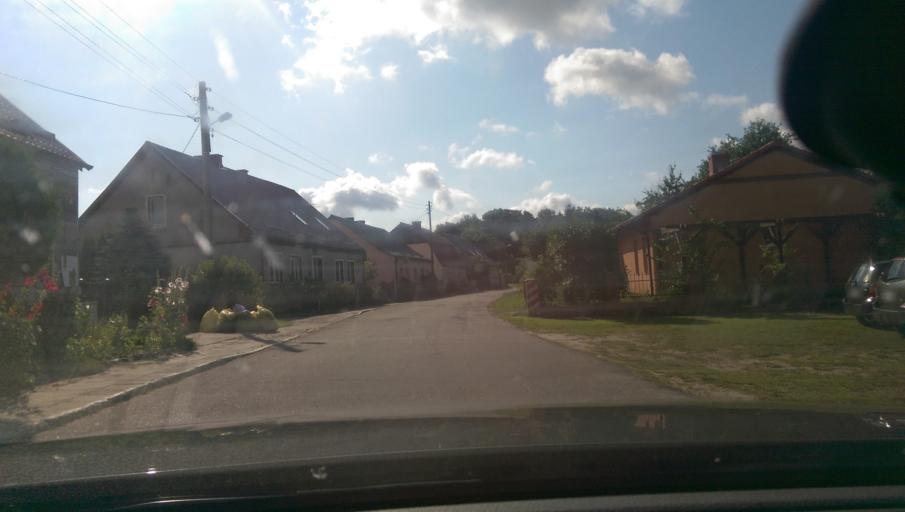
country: PL
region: West Pomeranian Voivodeship
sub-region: Powiat walecki
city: Walcz
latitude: 53.3793
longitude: 16.5005
